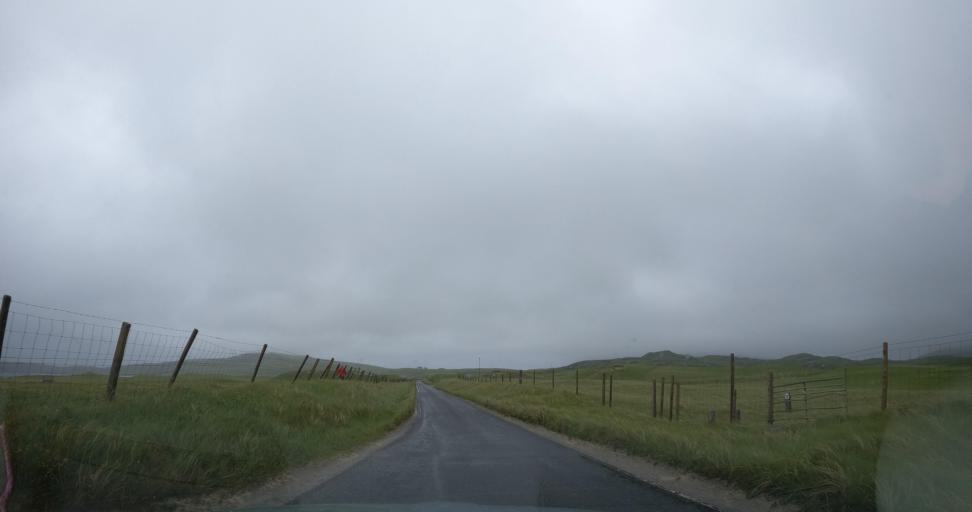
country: GB
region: Scotland
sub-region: Eilean Siar
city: Barra
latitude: 56.9964
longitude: -7.5066
